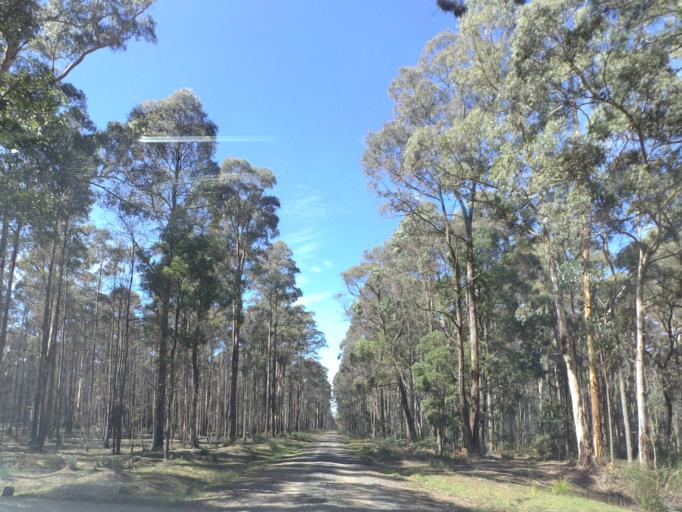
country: AU
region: Victoria
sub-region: Moorabool
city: Bacchus Marsh
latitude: -37.4030
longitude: 144.3231
